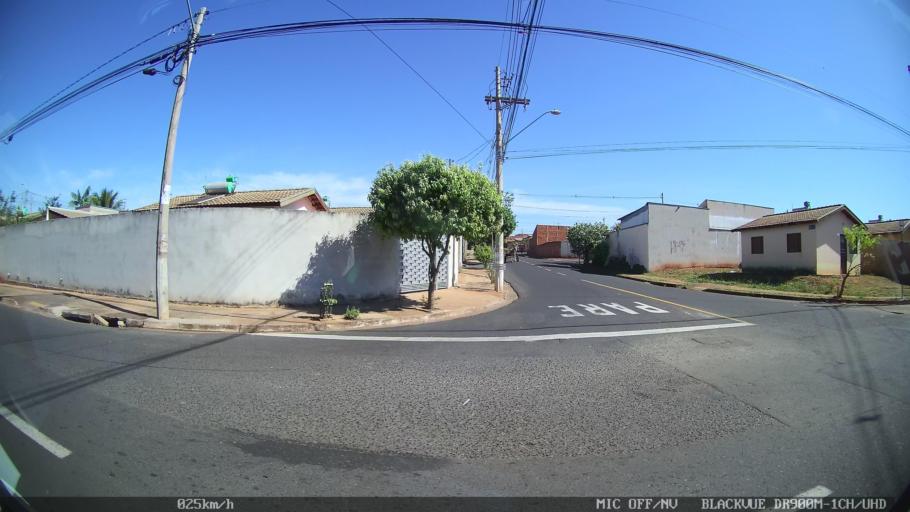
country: BR
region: Sao Paulo
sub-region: Sao Jose Do Rio Preto
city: Sao Jose do Rio Preto
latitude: -20.7435
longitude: -49.4088
